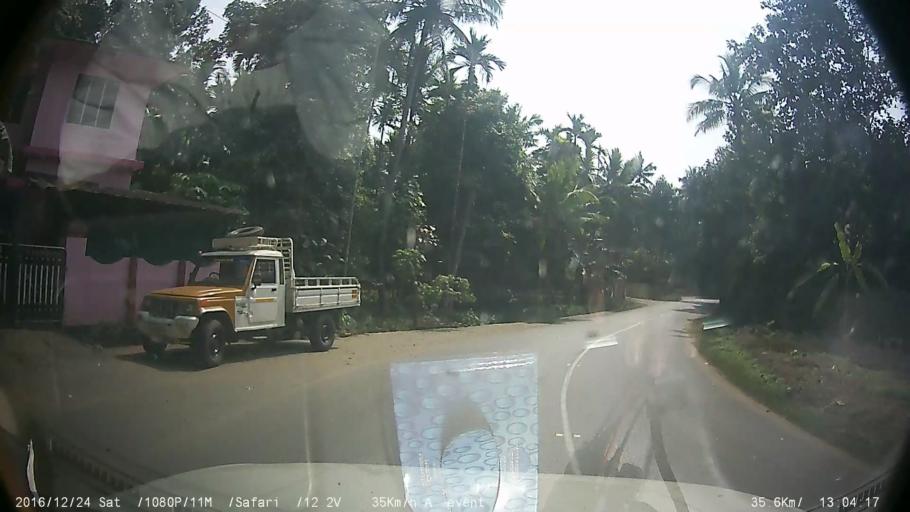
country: IN
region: Kerala
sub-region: Ernakulam
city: Muvattupuzha
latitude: 9.8907
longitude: 76.5935
